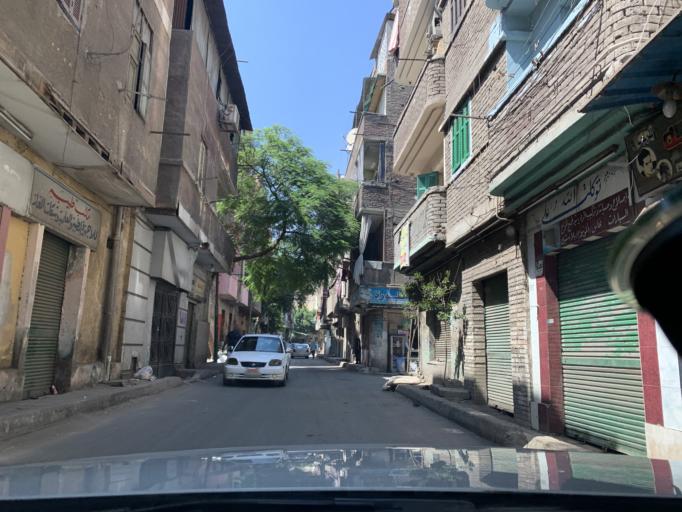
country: EG
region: Muhafazat al Qahirah
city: Cairo
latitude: 30.0708
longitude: 31.2558
